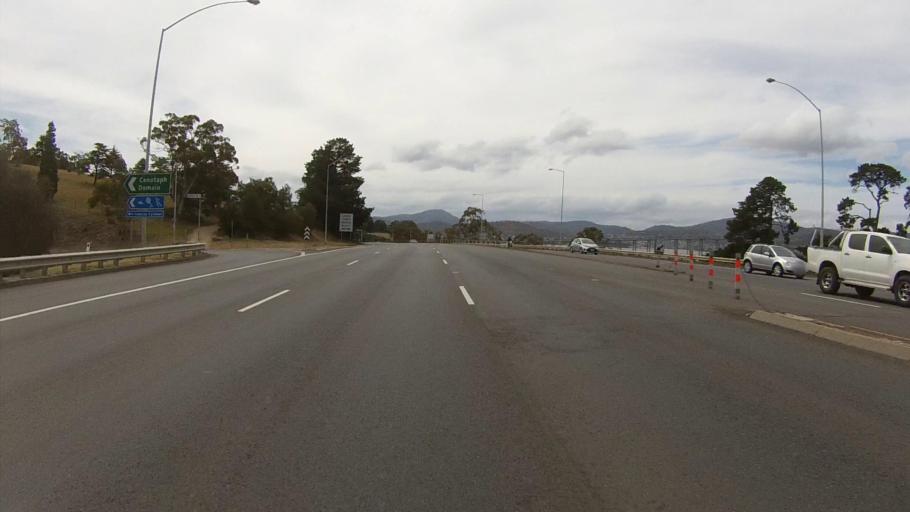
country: AU
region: Tasmania
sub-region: Hobart
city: Hobart
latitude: -42.8751
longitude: 147.3340
